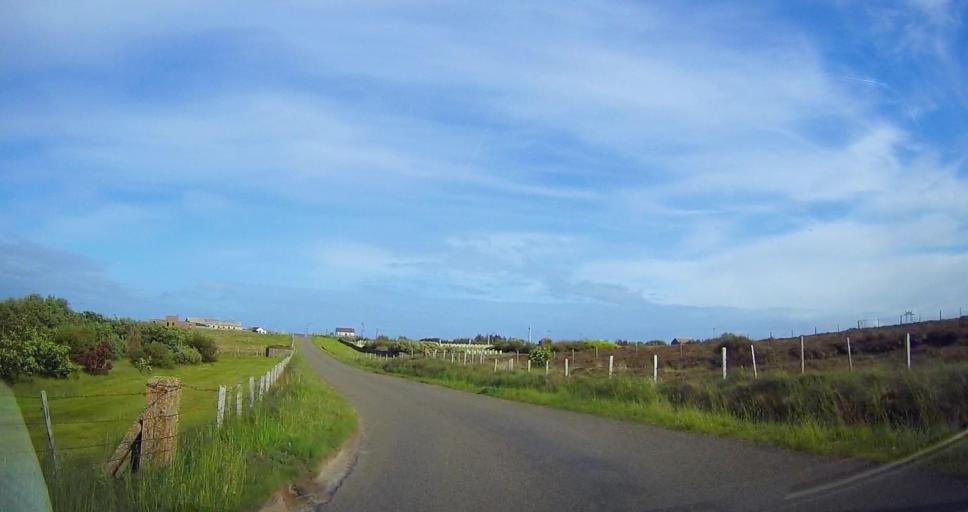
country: GB
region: Scotland
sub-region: Orkney Islands
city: Stromness
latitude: 58.8345
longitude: -3.2131
